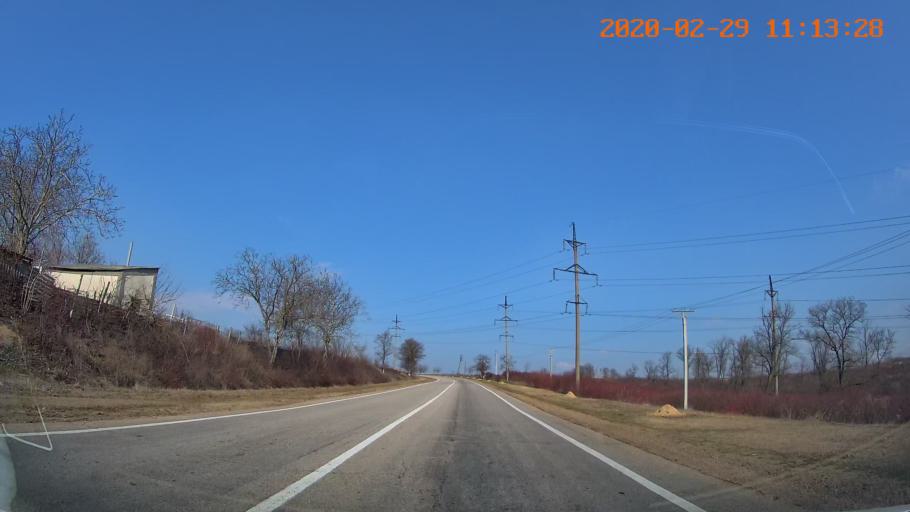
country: MD
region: Telenesti
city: Dubasari
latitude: 47.2724
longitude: 29.1810
